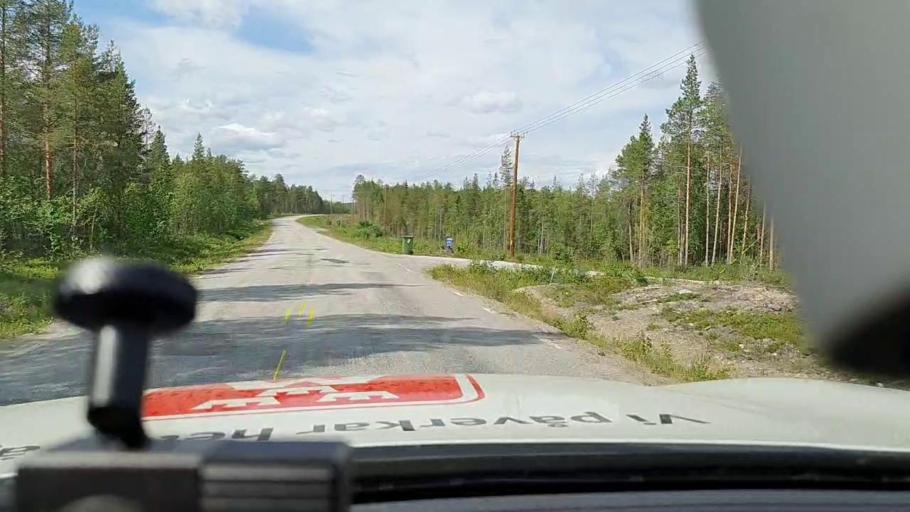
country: SE
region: Norrbotten
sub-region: Jokkmokks Kommun
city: Jokkmokk
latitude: 66.6234
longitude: 19.6909
